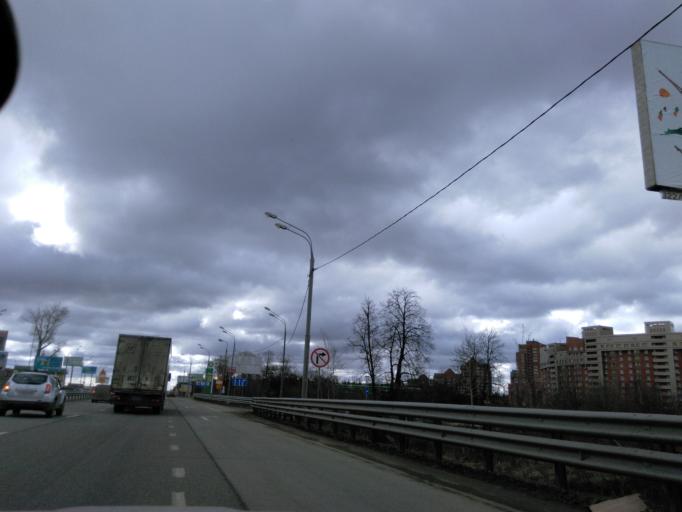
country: RU
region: Moskovskaya
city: Rzhavki
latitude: 55.9968
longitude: 37.2523
